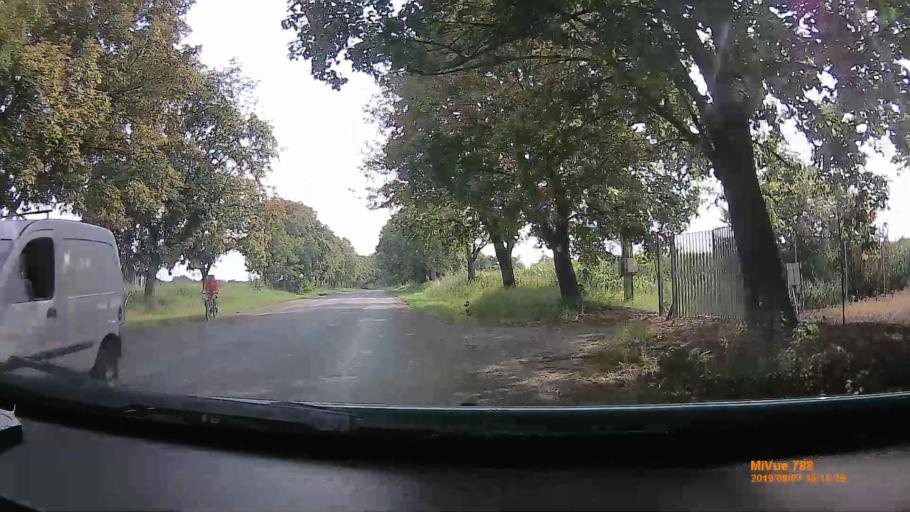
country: HU
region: Borsod-Abauj-Zemplen
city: Gonc
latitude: 48.4694
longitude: 21.2549
